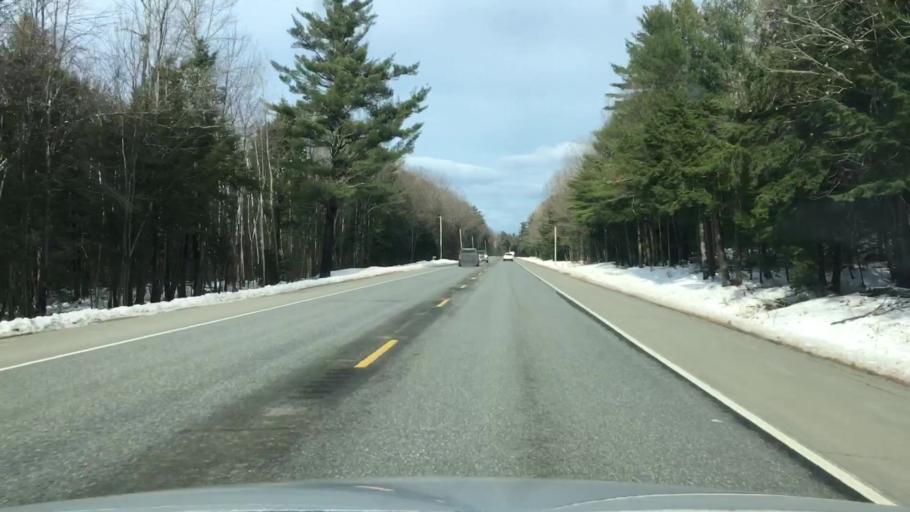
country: US
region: Maine
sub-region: Kennebec County
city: Monmouth
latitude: 44.2421
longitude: -70.0677
